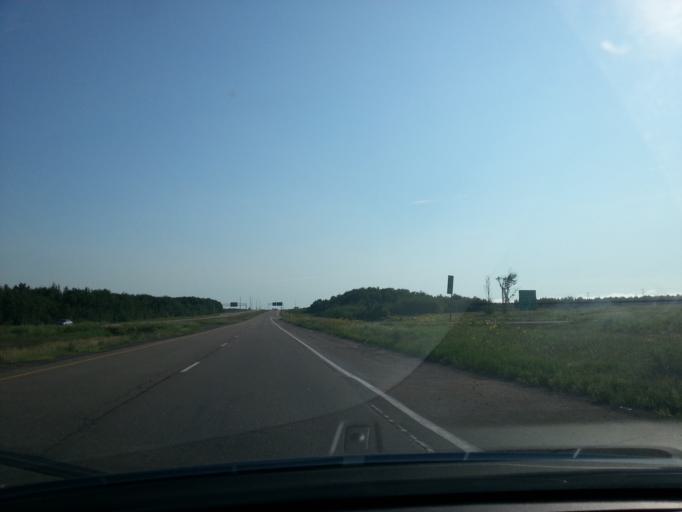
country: CA
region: New Brunswick
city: Dieppe
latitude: 46.1184
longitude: -64.6938
